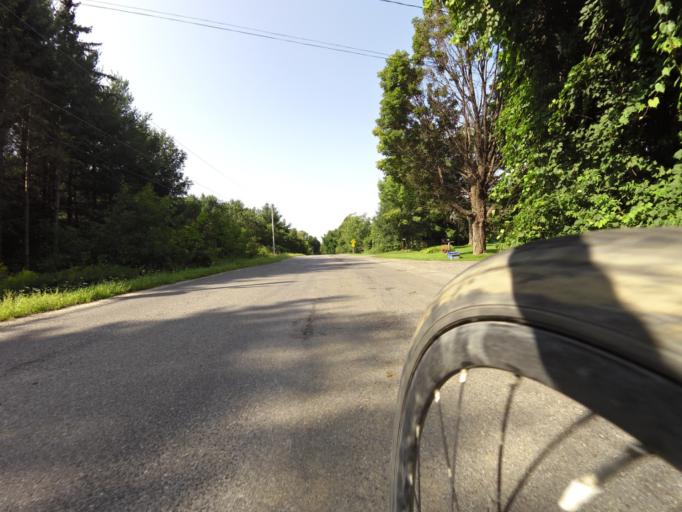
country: CA
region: Ontario
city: Kingston
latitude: 44.3333
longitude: -76.6666
